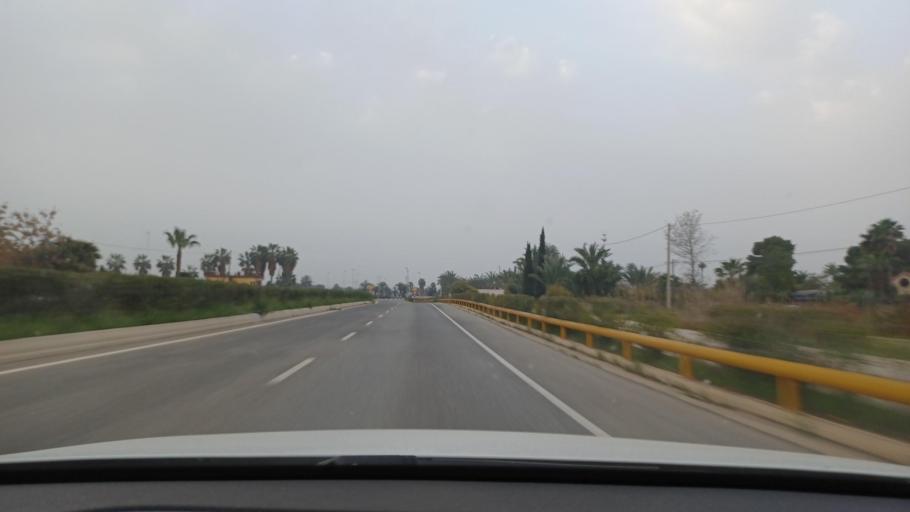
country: ES
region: Valencia
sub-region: Provincia de Alicante
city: Elche
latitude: 38.1826
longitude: -0.7017
